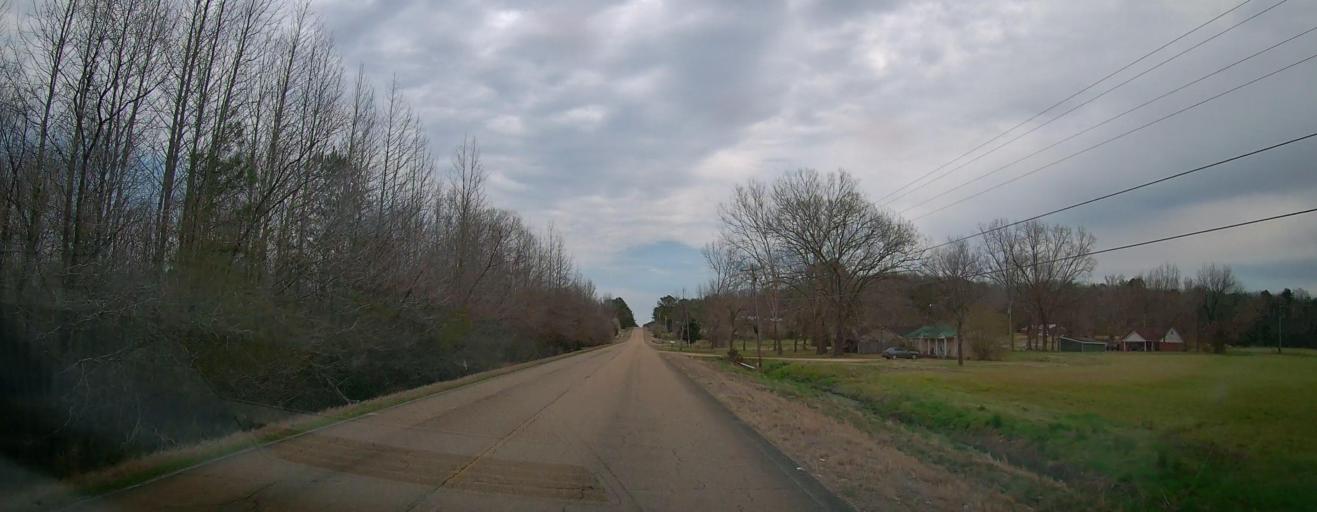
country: US
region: Mississippi
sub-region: Itawamba County
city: Fulton
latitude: 34.2249
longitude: -88.2267
